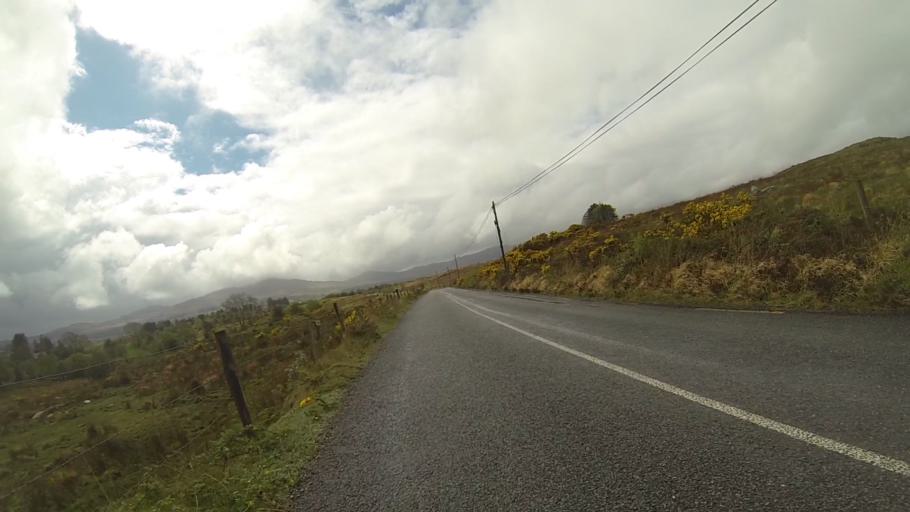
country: IE
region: Munster
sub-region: Ciarrai
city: Kenmare
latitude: 51.9010
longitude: -9.7457
